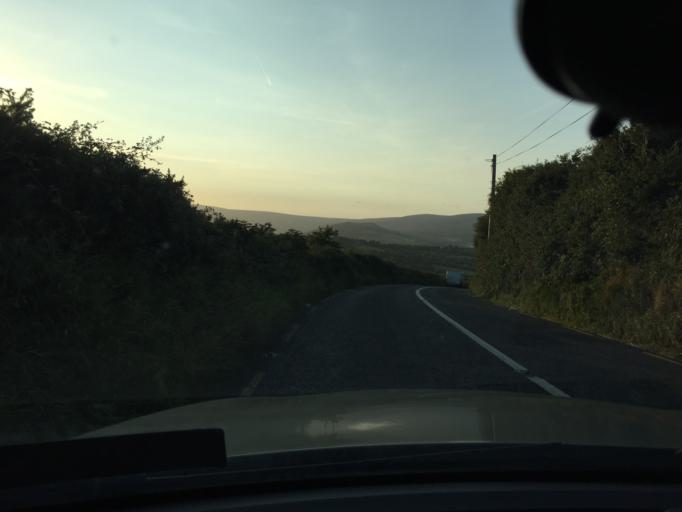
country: IE
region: Leinster
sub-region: Wicklow
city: Kilmacanoge
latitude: 53.1504
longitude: -6.1636
